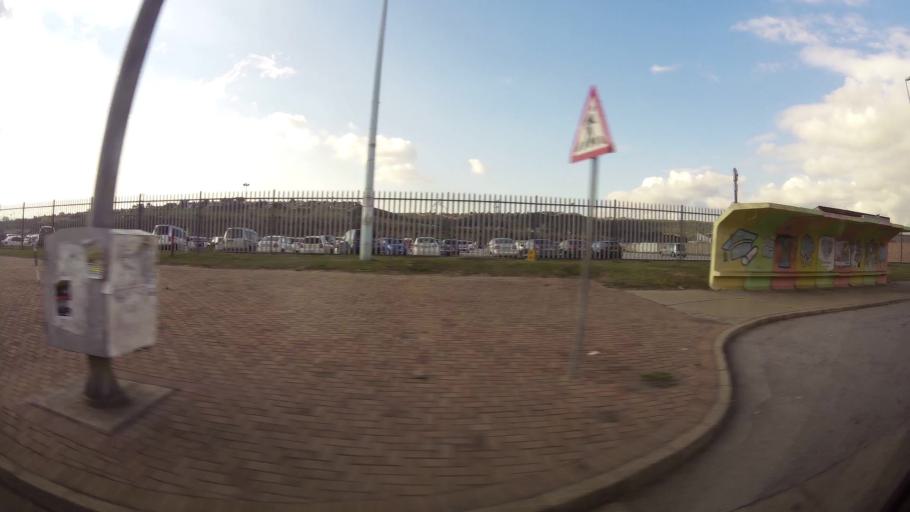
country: ZA
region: Eastern Cape
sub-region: Nelson Mandela Bay Metropolitan Municipality
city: Uitenhage
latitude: -33.7836
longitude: 25.4195
